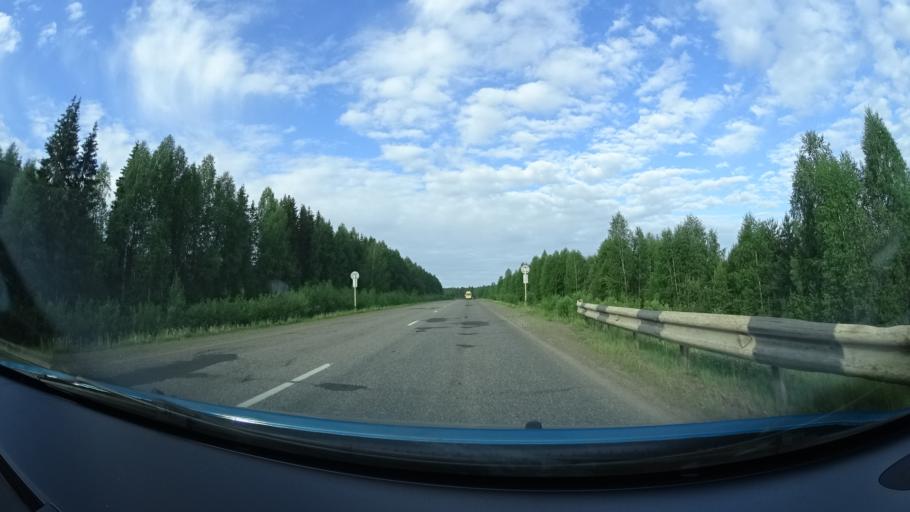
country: RU
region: Perm
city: Osa
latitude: 57.4436
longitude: 55.6397
